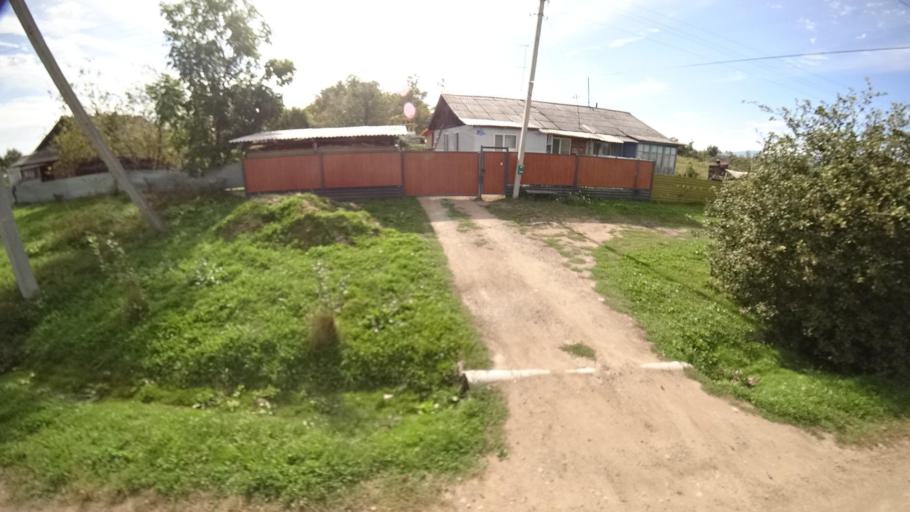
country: RU
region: Primorskiy
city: Dostoyevka
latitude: 44.3012
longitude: 133.4634
